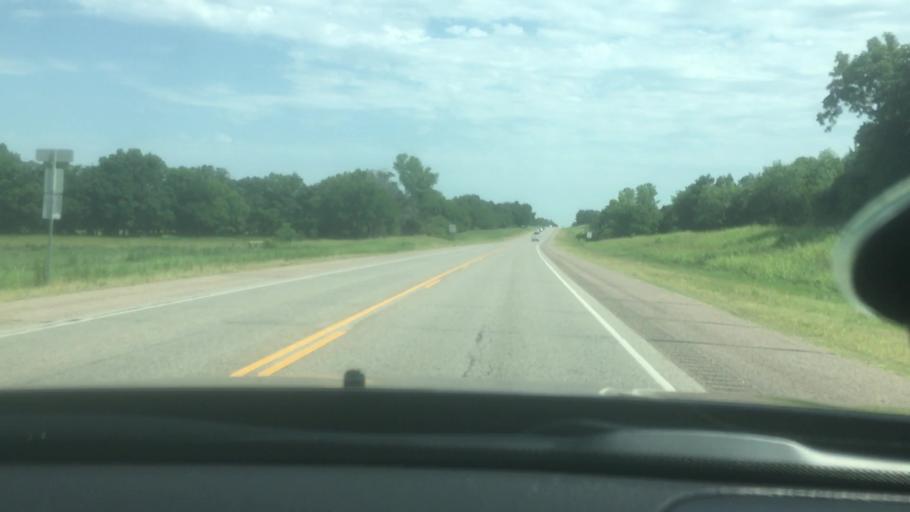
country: US
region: Oklahoma
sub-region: Seminole County
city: Konawa
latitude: 34.9940
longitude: -96.9312
